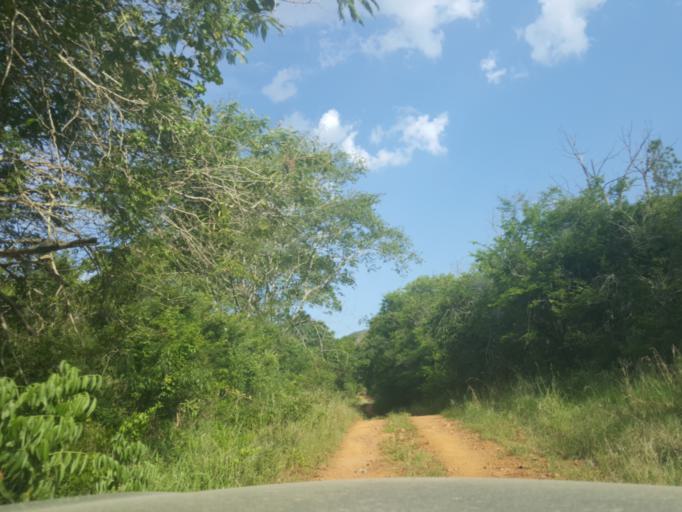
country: ZA
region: Limpopo
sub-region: Mopani District Municipality
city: Hoedspruit
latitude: -24.5946
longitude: 30.8463
